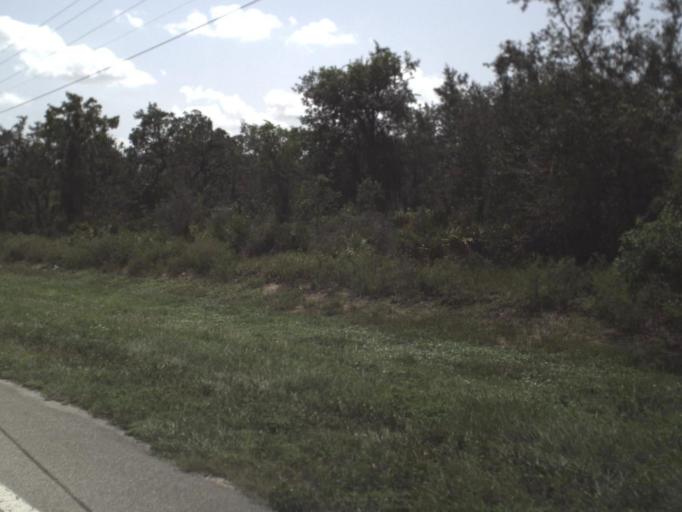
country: US
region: Florida
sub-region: Highlands County
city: Sebring
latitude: 27.4600
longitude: -81.4291
